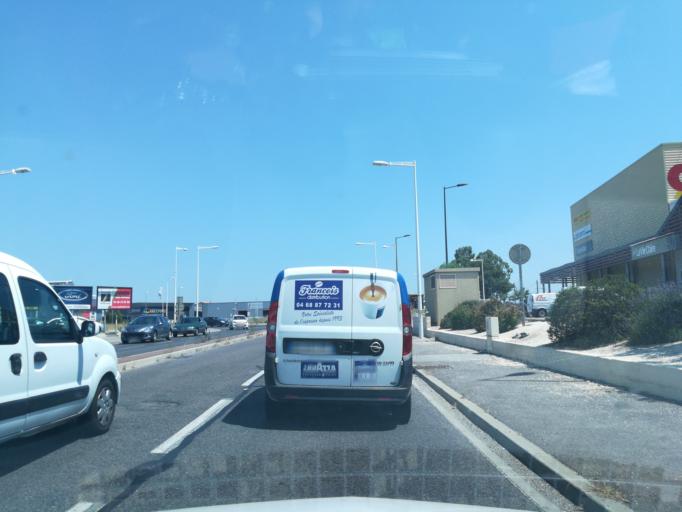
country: FR
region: Languedoc-Roussillon
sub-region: Departement des Pyrenees-Orientales
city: Pia
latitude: 42.7338
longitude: 2.8887
